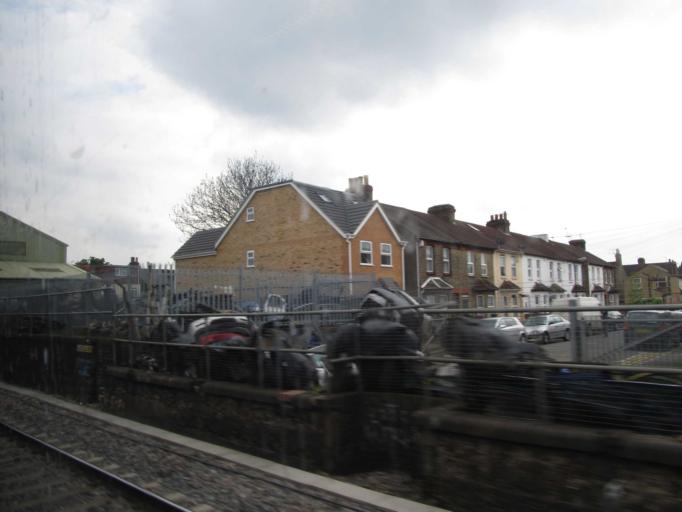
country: GB
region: England
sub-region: Slough
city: Slough
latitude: 51.5106
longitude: -0.5818
